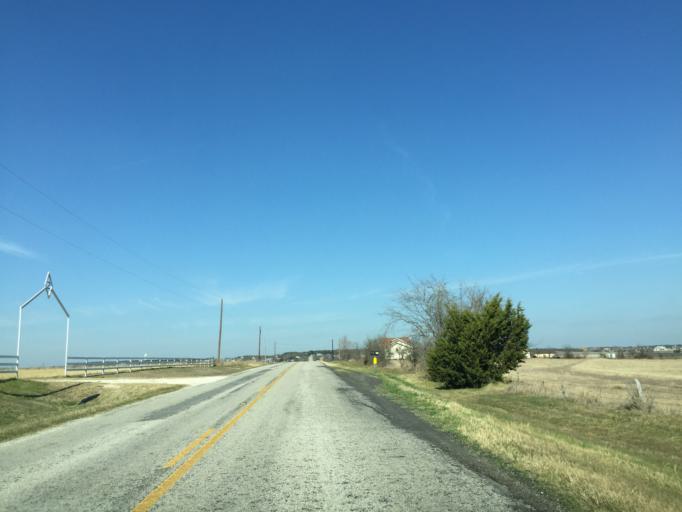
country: US
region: Texas
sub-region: Williamson County
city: Serenada
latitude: 30.7213
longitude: -97.5816
